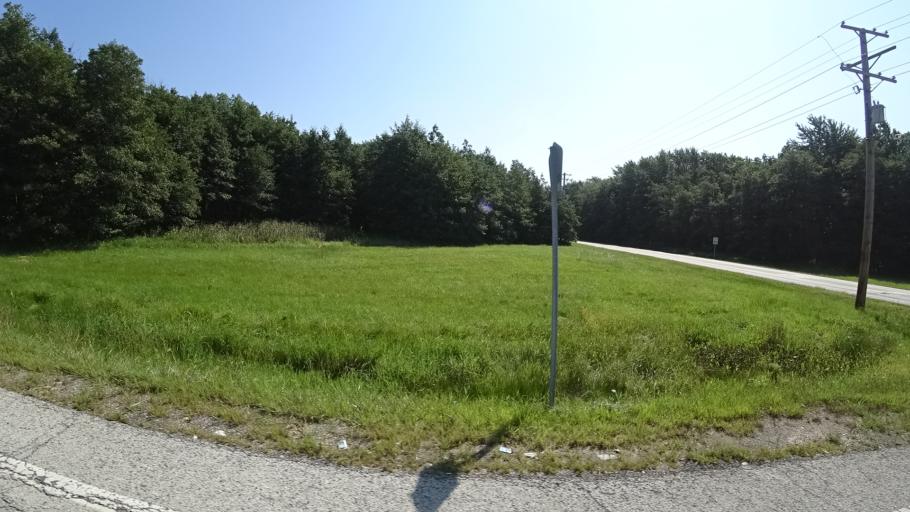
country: US
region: Illinois
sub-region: Cook County
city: Country Club Hills
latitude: 41.5572
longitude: -87.7524
